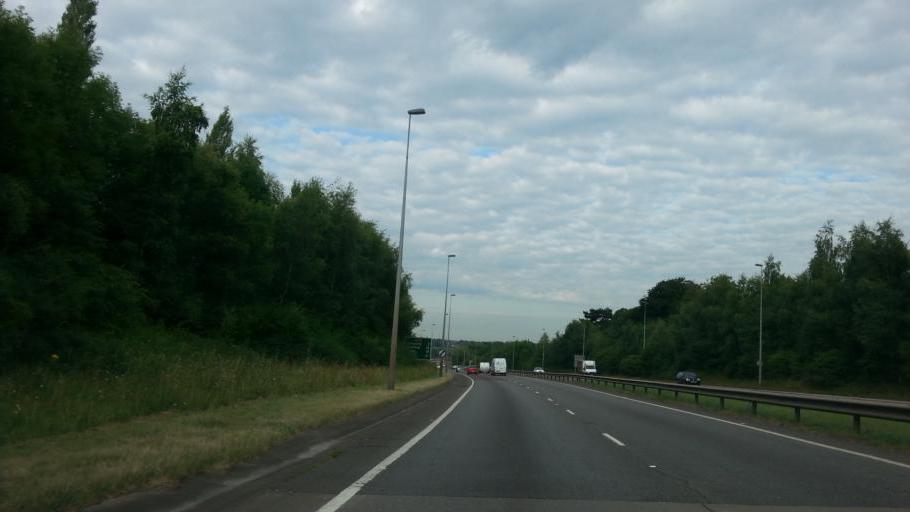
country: GB
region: England
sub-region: Staffordshire
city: Uttoxeter
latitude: 52.9097
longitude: -1.8333
